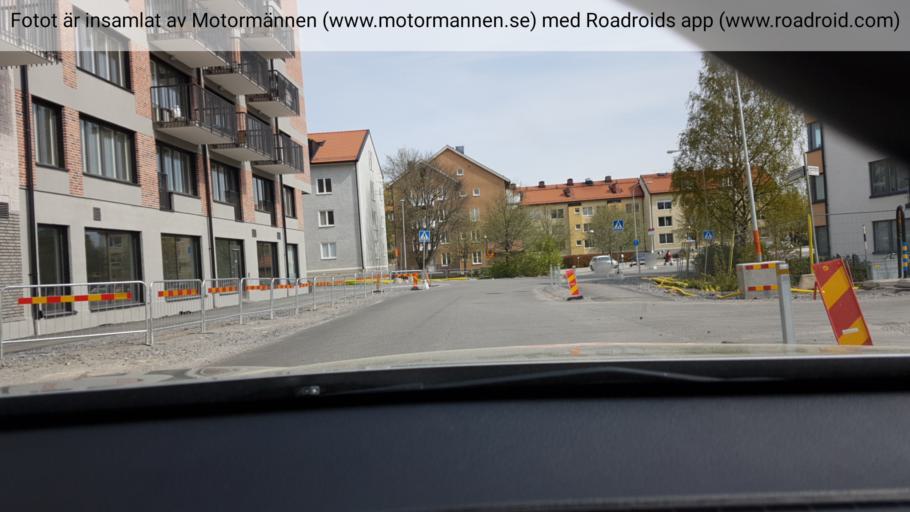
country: SE
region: Stockholm
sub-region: Huddinge Kommun
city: Huddinge
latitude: 59.2323
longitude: 17.9912
